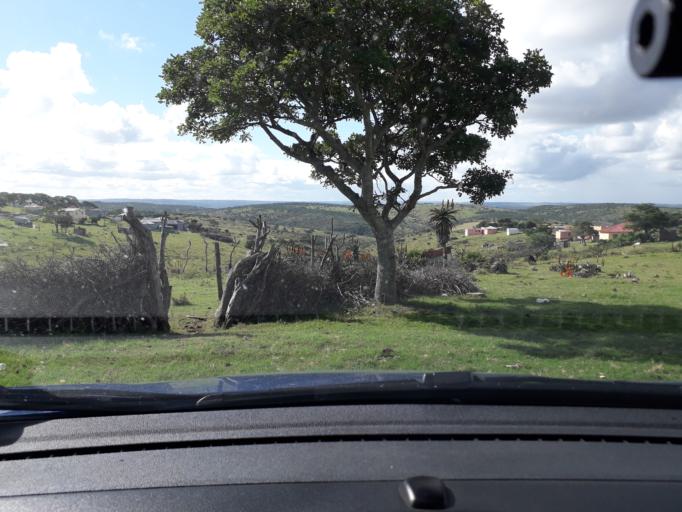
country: ZA
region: Eastern Cape
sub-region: Buffalo City Metropolitan Municipality
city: Bhisho
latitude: -33.1130
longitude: 27.4277
